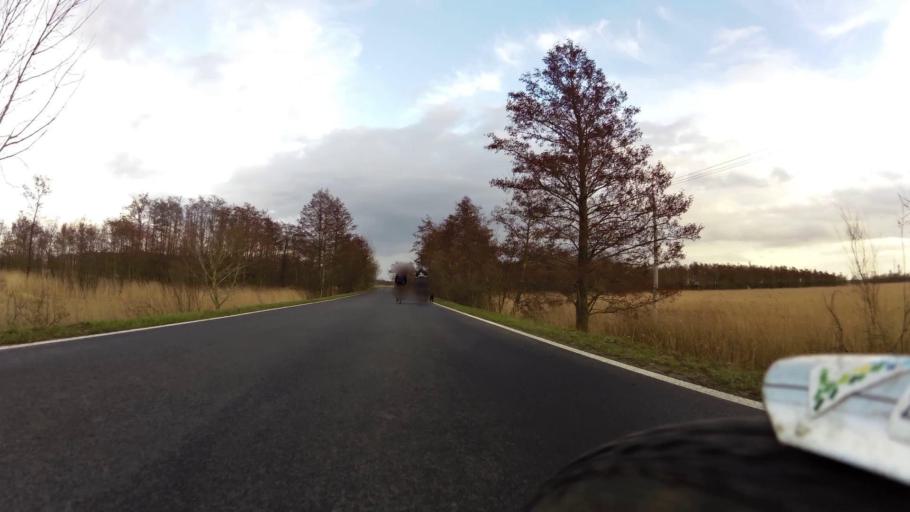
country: PL
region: West Pomeranian Voivodeship
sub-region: Powiat kamienski
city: Kamien Pomorski
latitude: 53.9181
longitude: 14.7507
